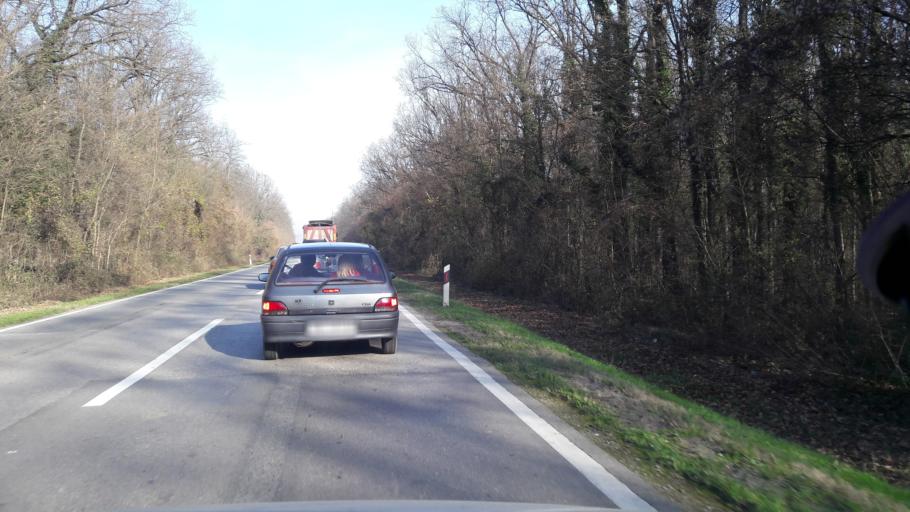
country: HR
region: Vukovarsko-Srijemska
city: Gradiste
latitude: 45.1229
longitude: 18.7119
